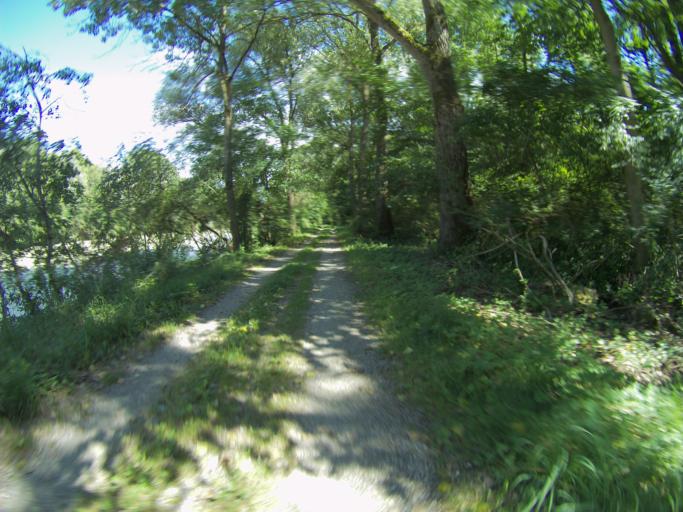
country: DE
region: Bavaria
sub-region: Upper Bavaria
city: Marzling
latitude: 48.4044
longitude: 11.7778
